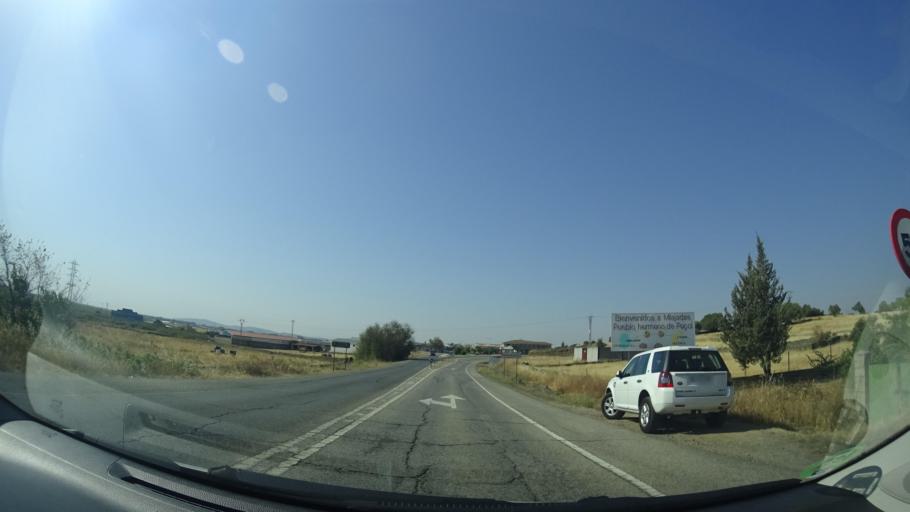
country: ES
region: Extremadura
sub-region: Provincia de Caceres
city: Miajadas
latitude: 39.1619
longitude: -5.8988
